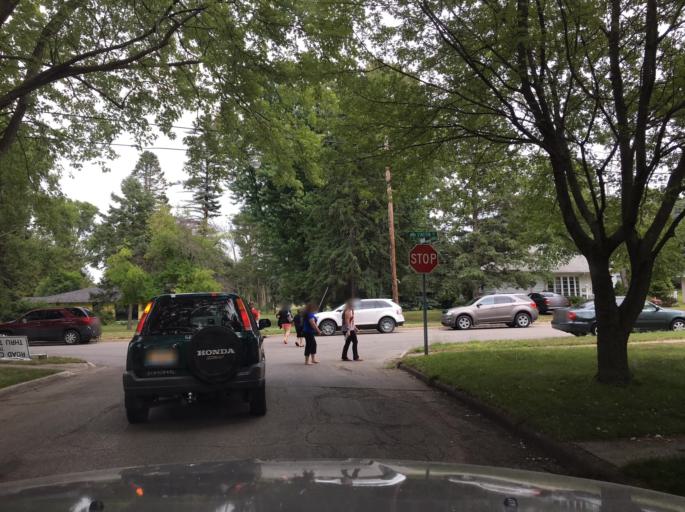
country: US
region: Michigan
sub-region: Mason County
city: Ludington
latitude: 43.9536
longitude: -86.4347
